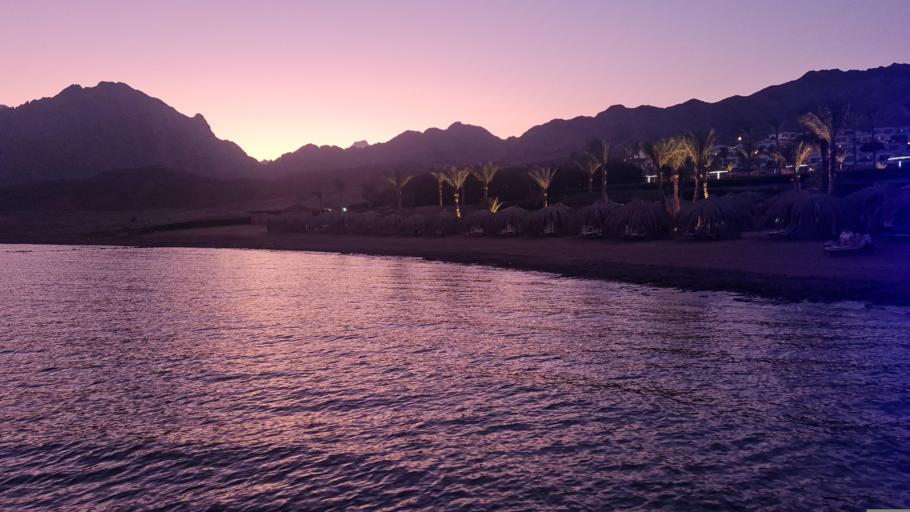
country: EG
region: South Sinai
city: Dhahab
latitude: 28.4573
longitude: 34.4720
